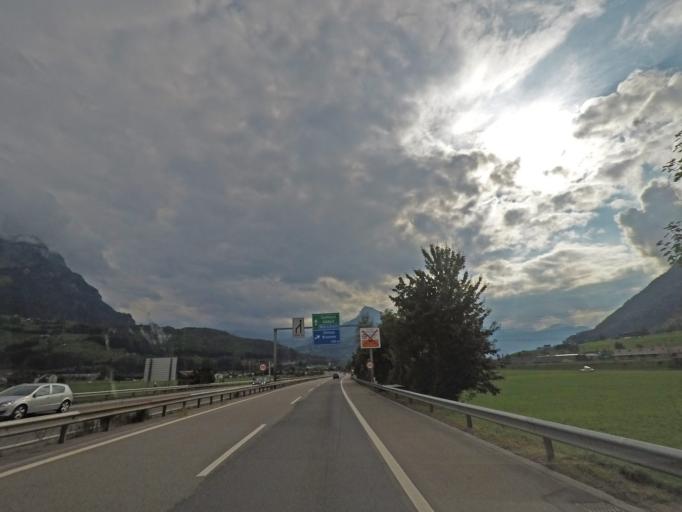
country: CH
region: Schwyz
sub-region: Bezirk Schwyz
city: Ingenbohl
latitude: 47.0114
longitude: 8.6242
